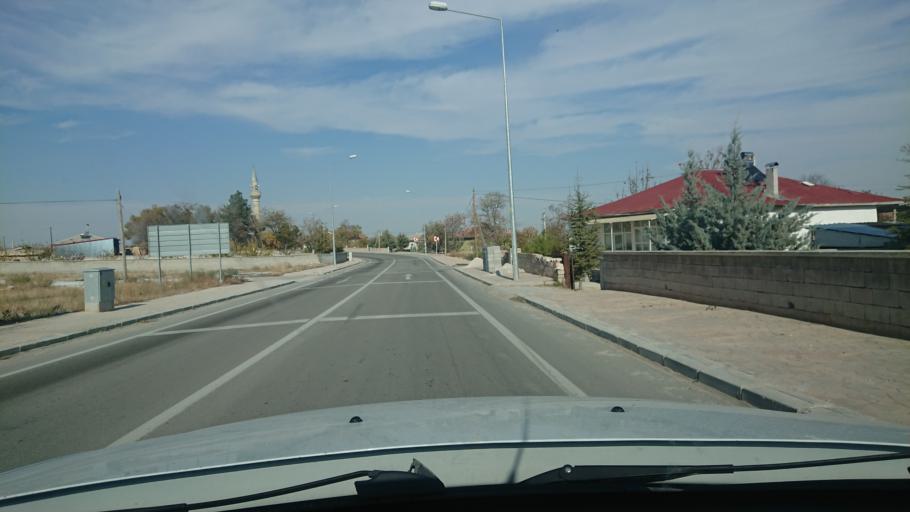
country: TR
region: Aksaray
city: Sultanhani
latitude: 38.2506
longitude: 33.4493
